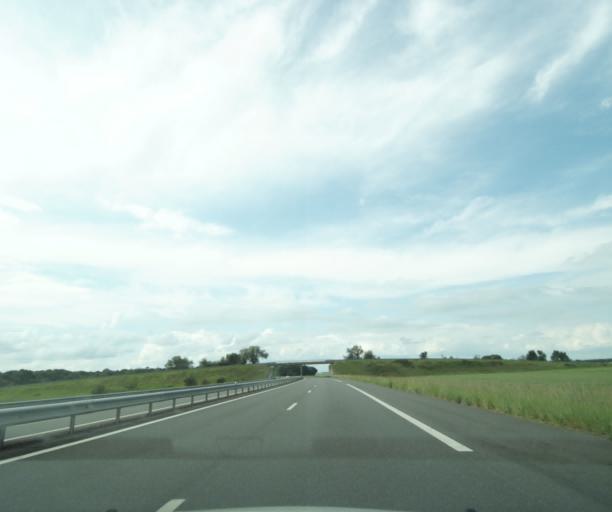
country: FR
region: Centre
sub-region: Departement du Cher
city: Levet
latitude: 46.9297
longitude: 2.4257
